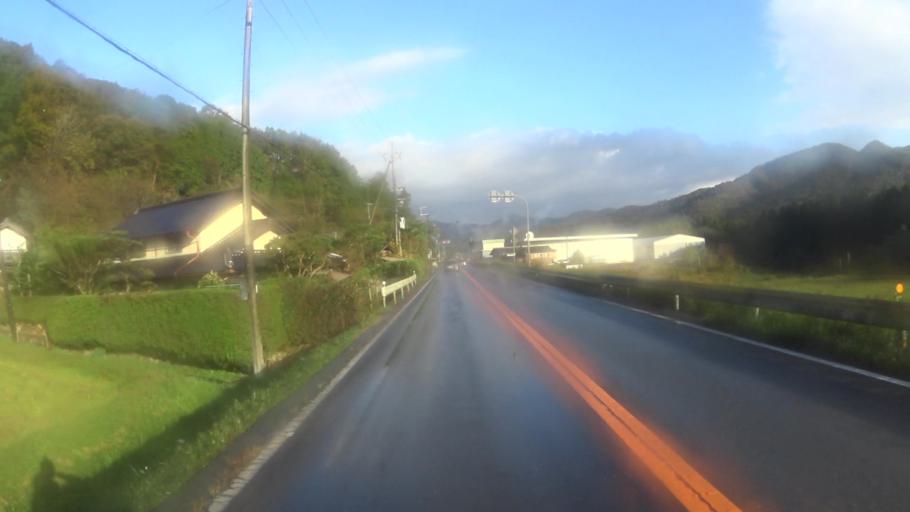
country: JP
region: Kyoto
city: Ayabe
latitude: 35.2374
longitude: 135.2187
